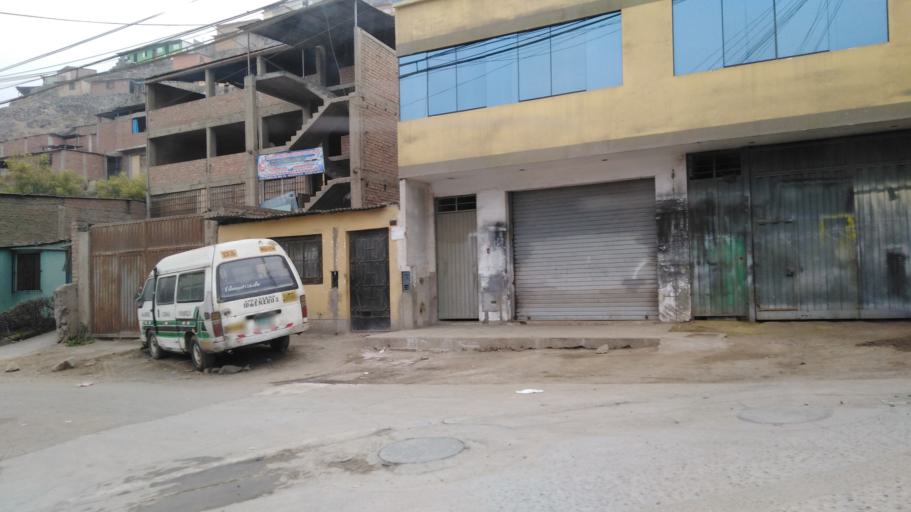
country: PE
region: Lima
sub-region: Lima
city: La Molina
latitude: -12.1445
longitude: -76.9376
